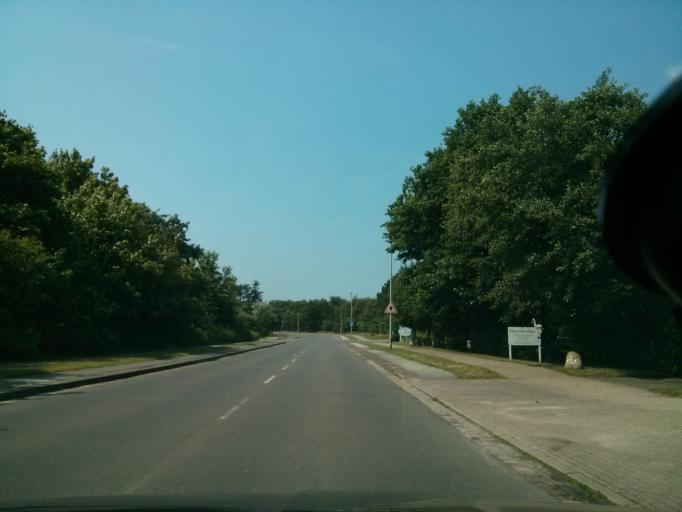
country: DE
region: Schleswig-Holstein
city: Sankt Peter-Ording
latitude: 54.3118
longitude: 8.6212
